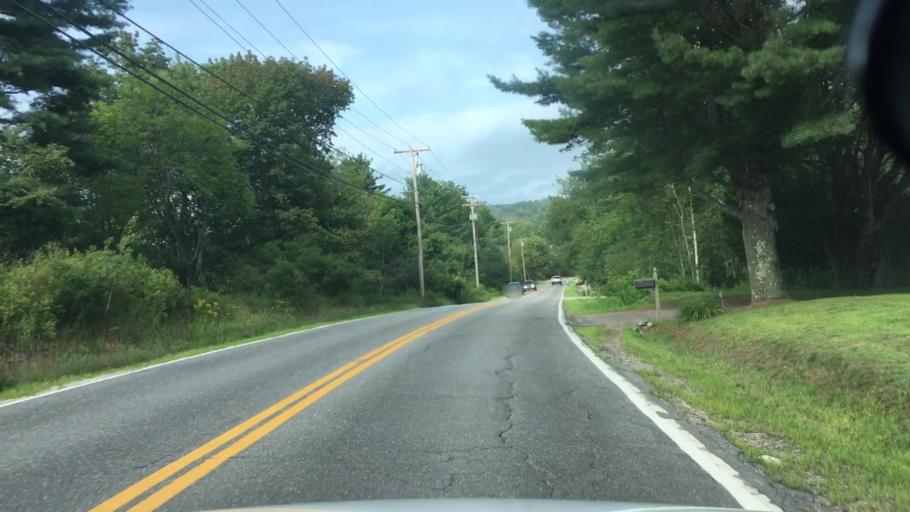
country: US
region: Maine
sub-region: Cumberland County
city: Harpswell Center
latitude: 43.7708
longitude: -69.9703
